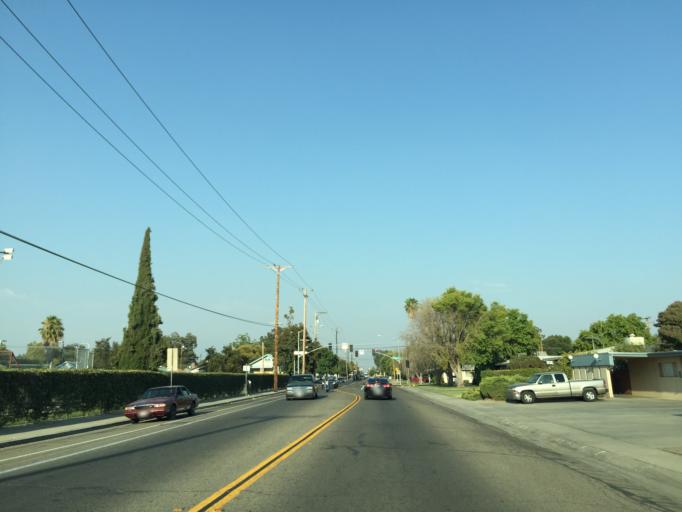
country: US
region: California
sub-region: Tulare County
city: Visalia
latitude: 36.3201
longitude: -119.2973
